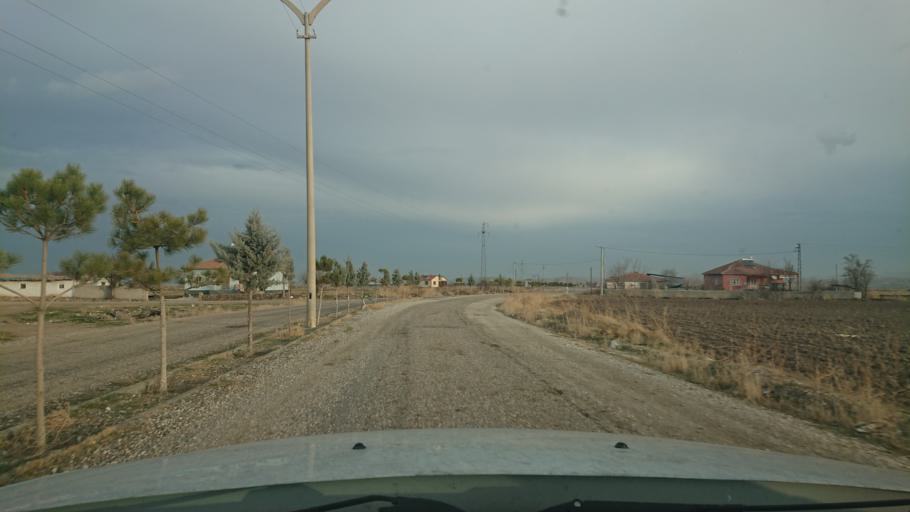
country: TR
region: Aksaray
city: Yesilova
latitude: 38.4228
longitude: 33.8343
